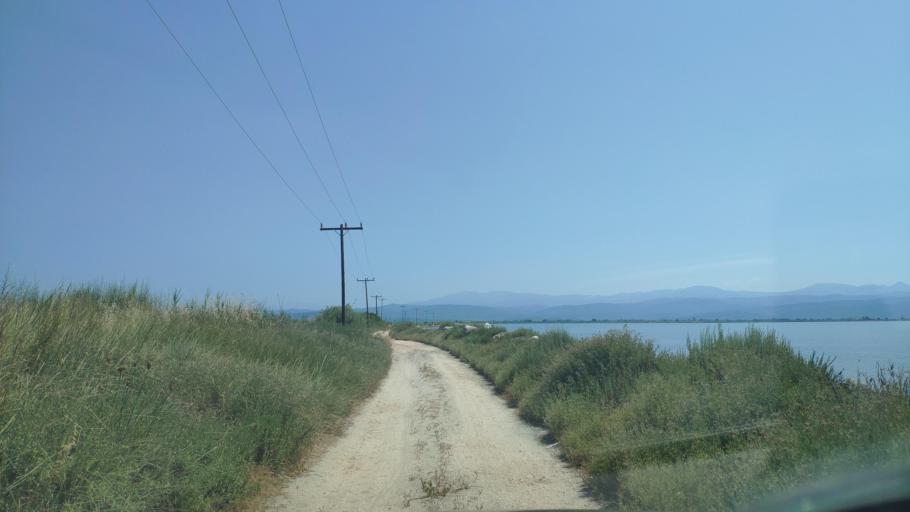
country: GR
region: Epirus
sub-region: Nomos Artas
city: Aneza
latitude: 39.0233
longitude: 20.9367
